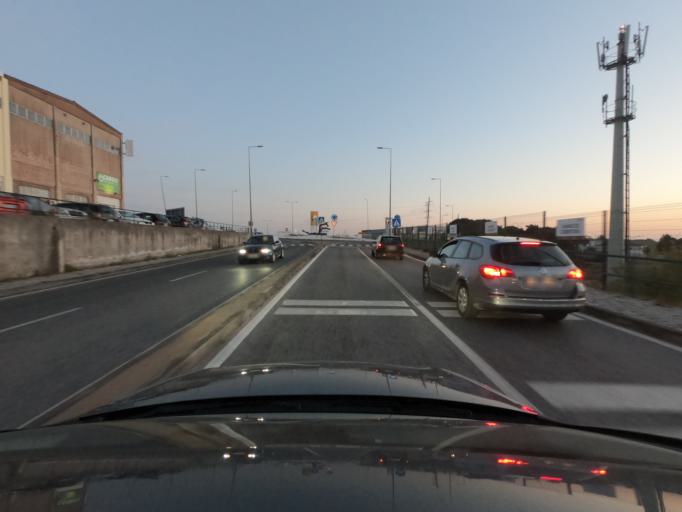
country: PT
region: Lisbon
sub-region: Sintra
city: Cacem
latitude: 38.7591
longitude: -9.3068
